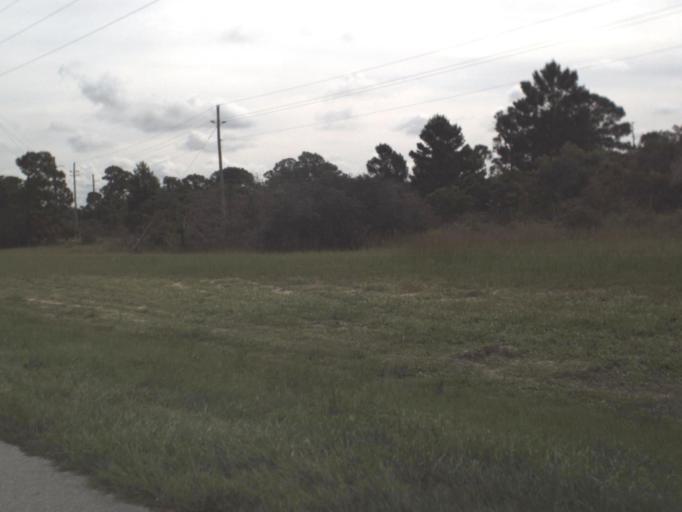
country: US
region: Florida
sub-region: Highlands County
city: Placid Lakes
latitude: 27.2110
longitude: -81.3516
